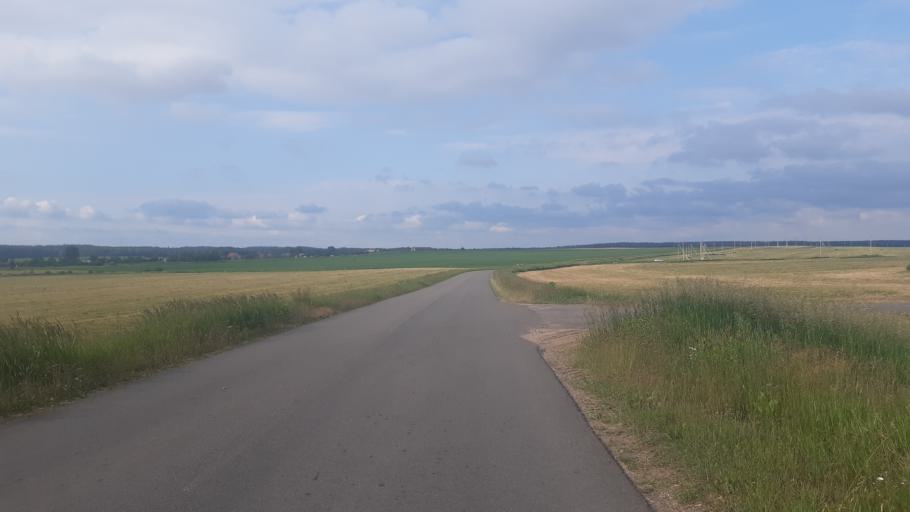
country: BY
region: Minsk
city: Horad Zhodzina
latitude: 54.1439
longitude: 28.2362
